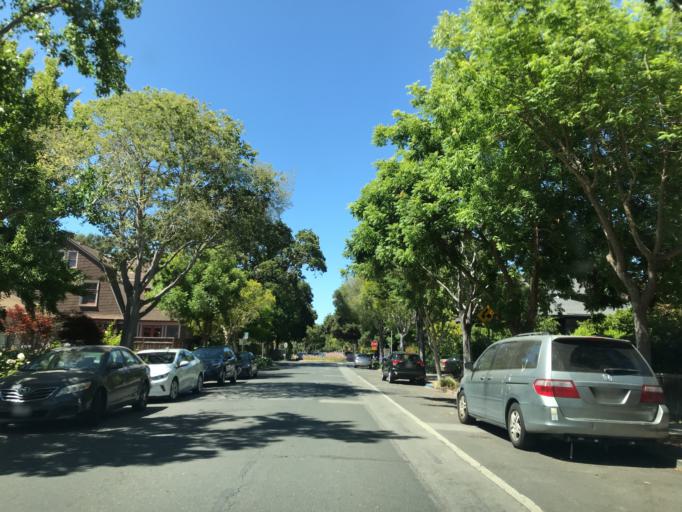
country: US
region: California
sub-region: Santa Clara County
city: Palo Alto
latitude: 37.4426
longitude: -122.1547
